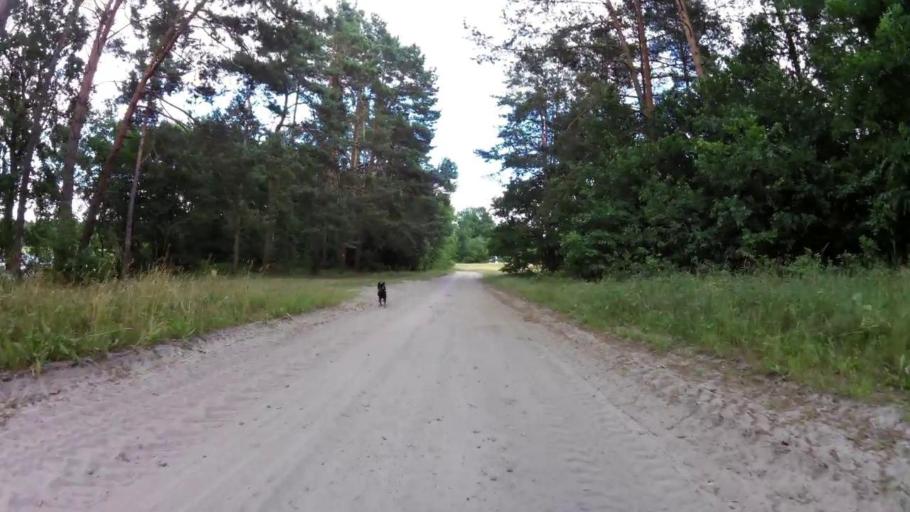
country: PL
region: West Pomeranian Voivodeship
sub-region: Powiat swidwinski
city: Swidwin
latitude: 53.6800
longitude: 15.7395
